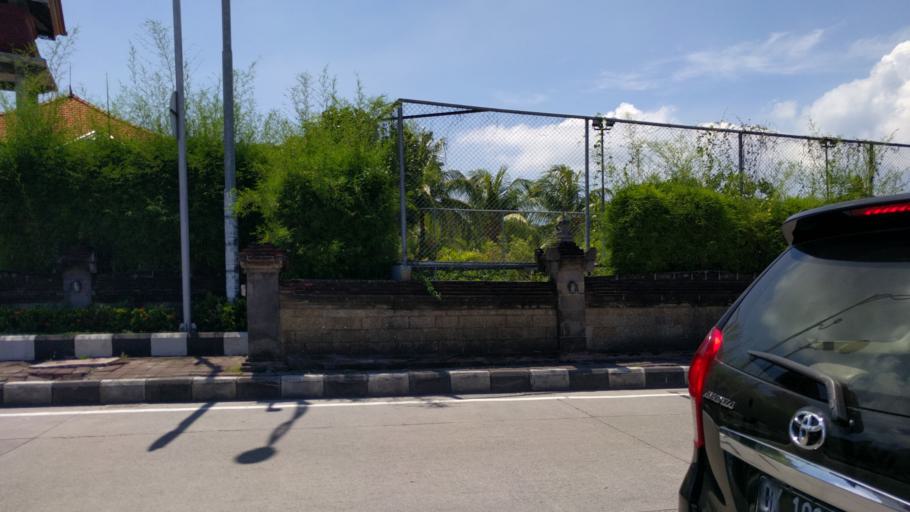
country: ID
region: Bali
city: Jabajero
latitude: -8.7238
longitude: 115.1815
